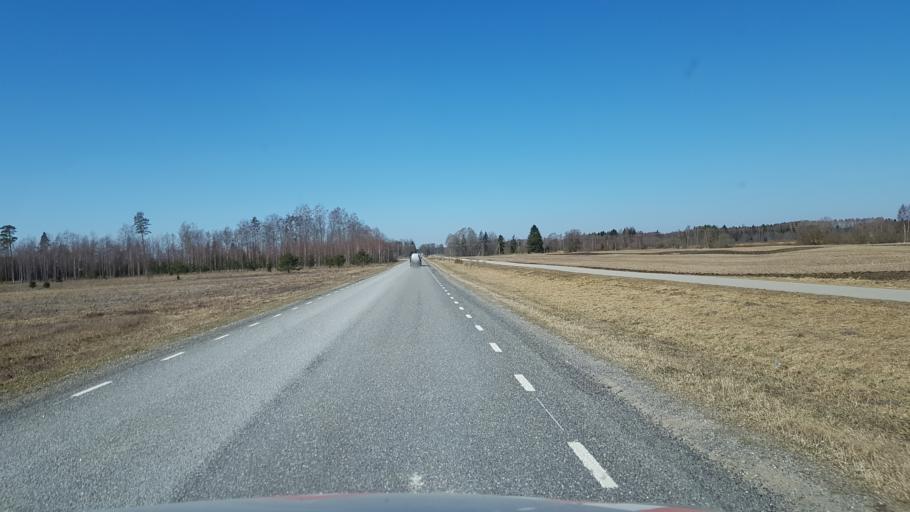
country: EE
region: Laeaene-Virumaa
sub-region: Rakke vald
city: Rakke
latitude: 58.9951
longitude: 26.2175
